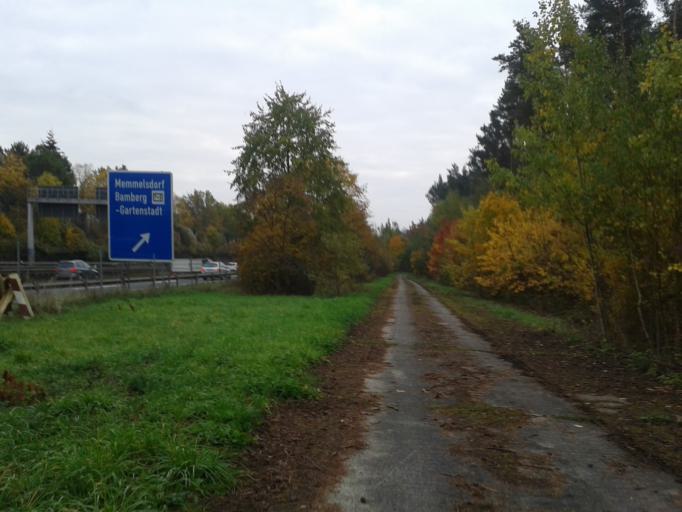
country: DE
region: Bavaria
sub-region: Upper Franconia
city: Gundelsheim
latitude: 49.9232
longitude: 10.9246
